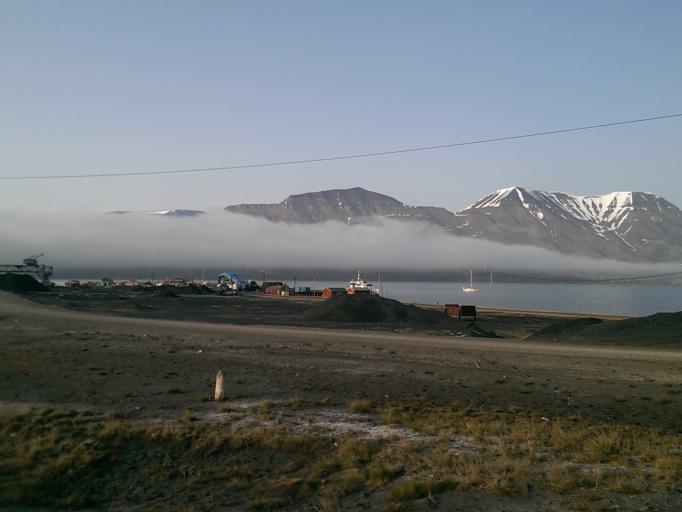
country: SJ
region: Svalbard
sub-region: Spitsbergen
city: Longyearbyen
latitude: 78.2412
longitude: 15.5308
